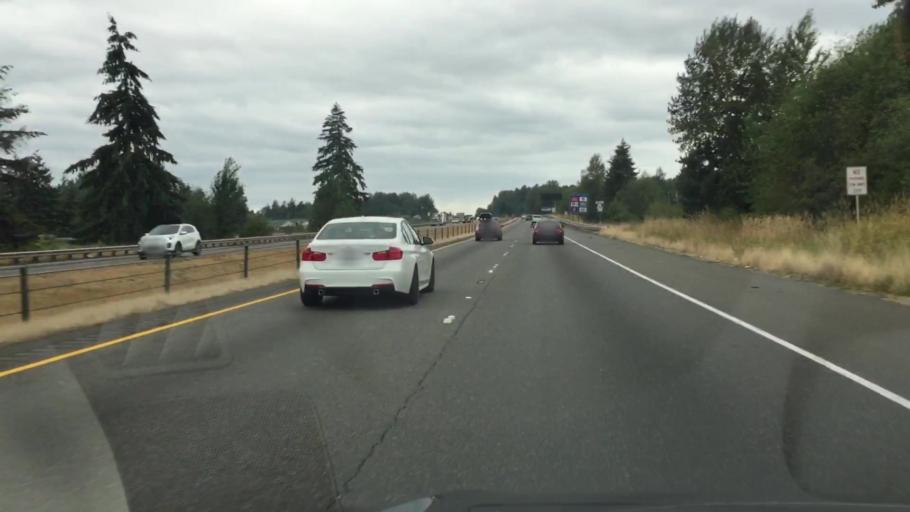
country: US
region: Washington
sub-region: Pierce County
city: Midland
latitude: 47.1591
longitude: -122.4085
